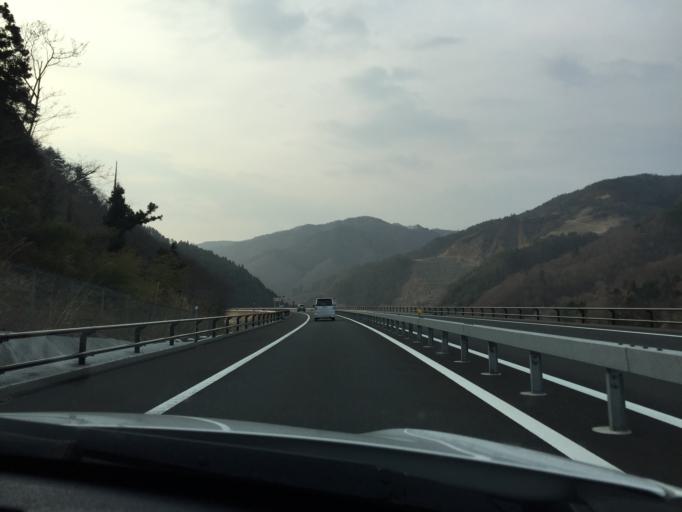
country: JP
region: Miyagi
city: Marumori
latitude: 37.7874
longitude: 140.7908
